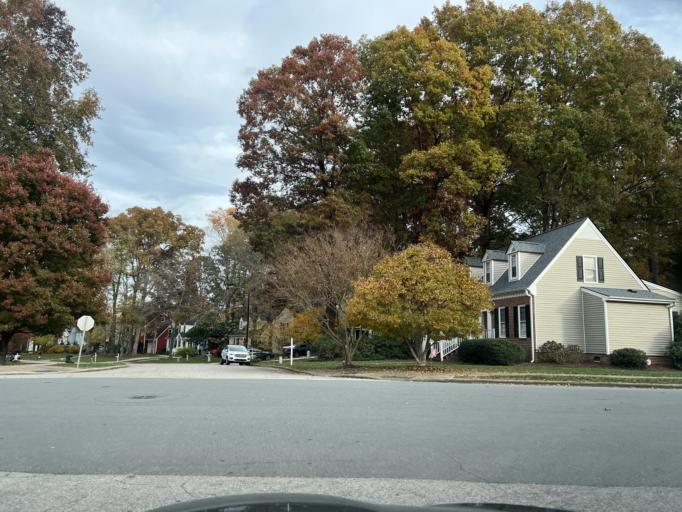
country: US
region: North Carolina
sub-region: Wake County
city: Wake Forest
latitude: 35.8956
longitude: -78.5902
